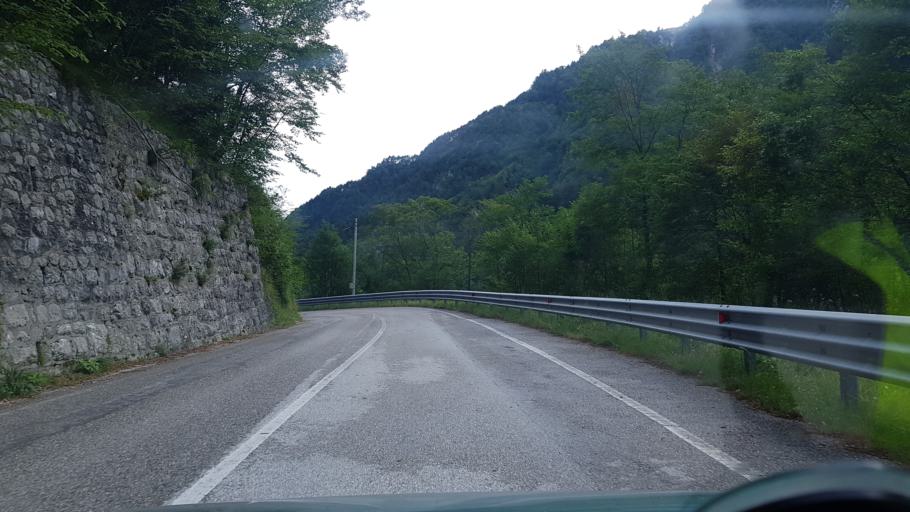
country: IT
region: Friuli Venezia Giulia
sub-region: Provincia di Udine
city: Lusevera
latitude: 46.2967
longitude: 13.2701
